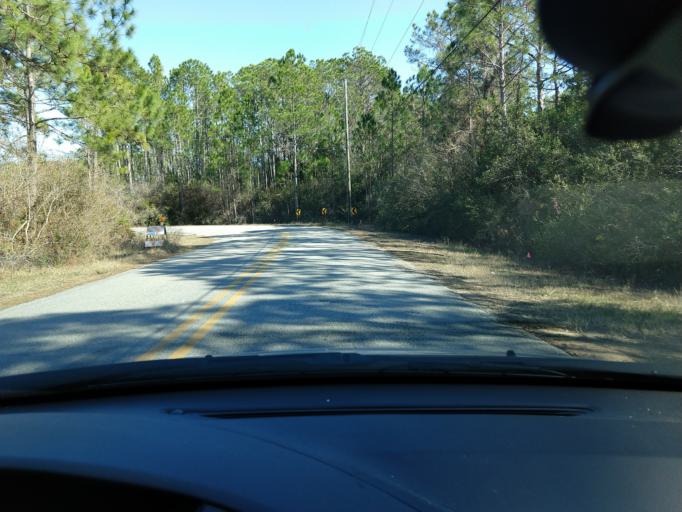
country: US
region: Florida
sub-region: Walton County
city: Miramar Beach
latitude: 30.3880
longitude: -86.3025
